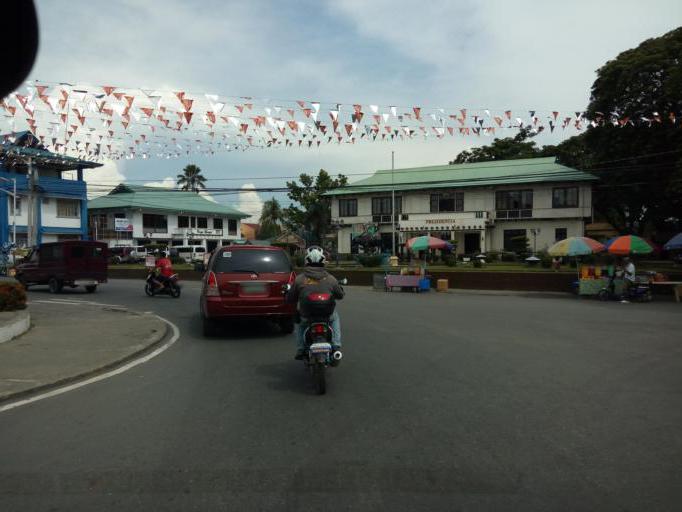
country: PH
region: Ilocos
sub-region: Province of Pangasinan
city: Rosales
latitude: 15.8928
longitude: 120.6326
